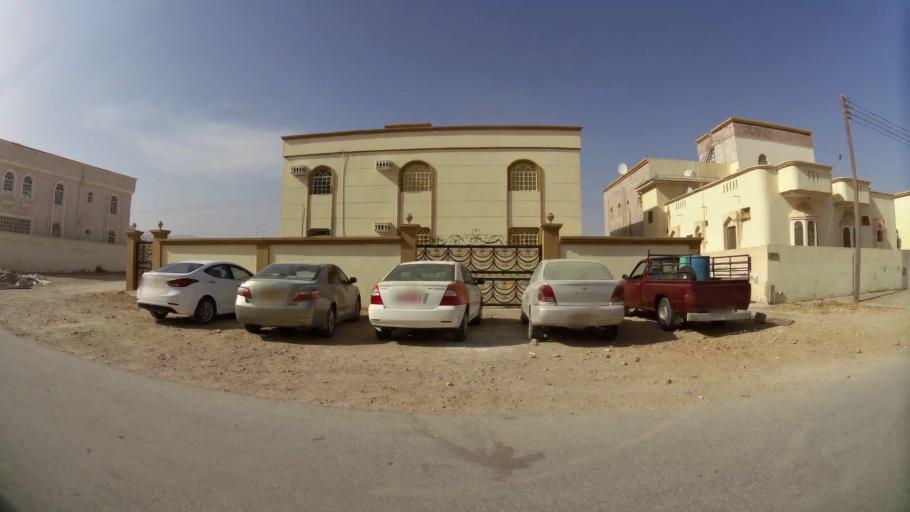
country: OM
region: Zufar
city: Salalah
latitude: 17.0147
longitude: 54.0113
